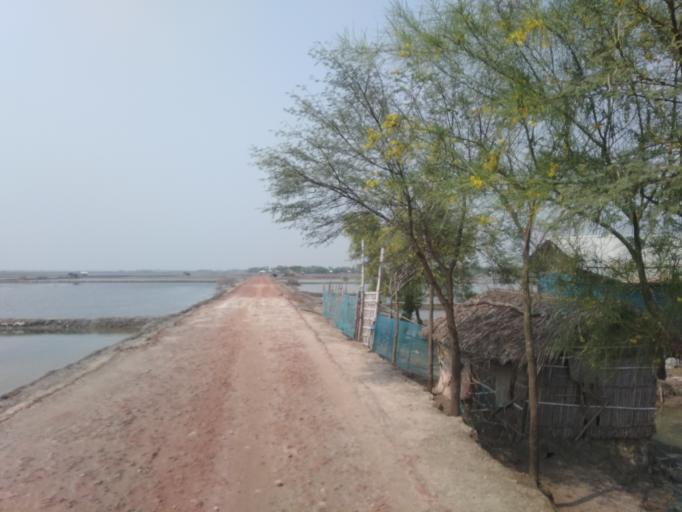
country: IN
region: West Bengal
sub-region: North 24 Parganas
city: Taki
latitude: 22.2913
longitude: 89.2720
